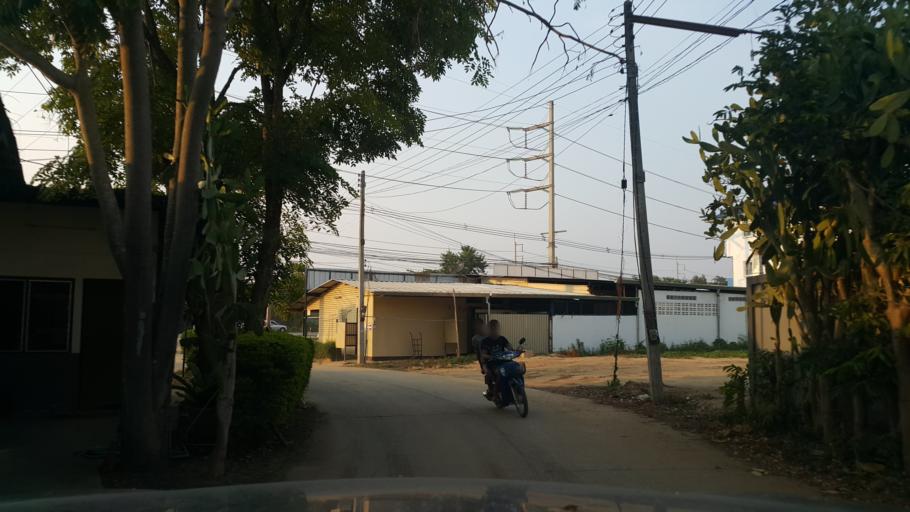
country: TH
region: Chiang Mai
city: Saraphi
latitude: 18.7259
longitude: 99.0175
